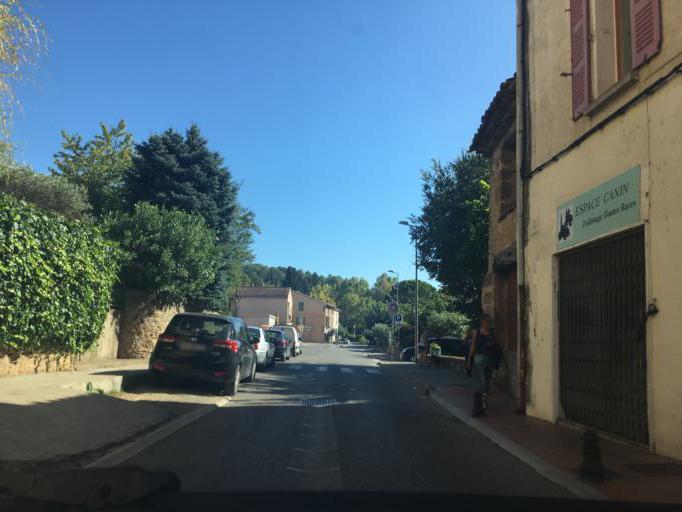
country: FR
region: Provence-Alpes-Cote d'Azur
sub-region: Departement du Var
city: Salernes
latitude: 43.5623
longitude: 6.2330
